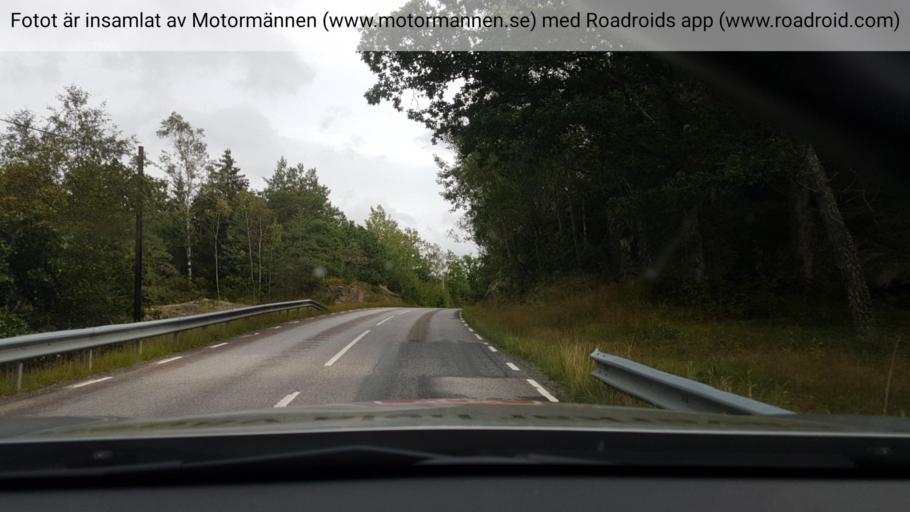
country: SE
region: Vaestra Goetaland
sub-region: Sotenas Kommun
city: Hunnebostrand
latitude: 58.5627
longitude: 11.3925
